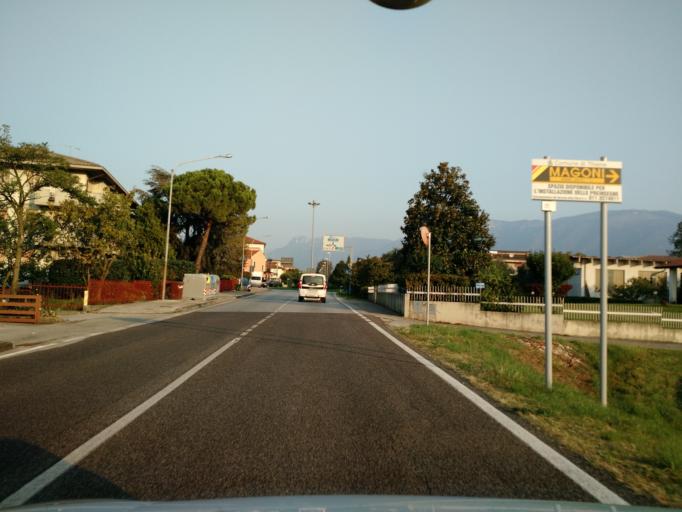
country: IT
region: Veneto
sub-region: Provincia di Vicenza
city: Thiene
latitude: 45.7093
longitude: 11.4941
